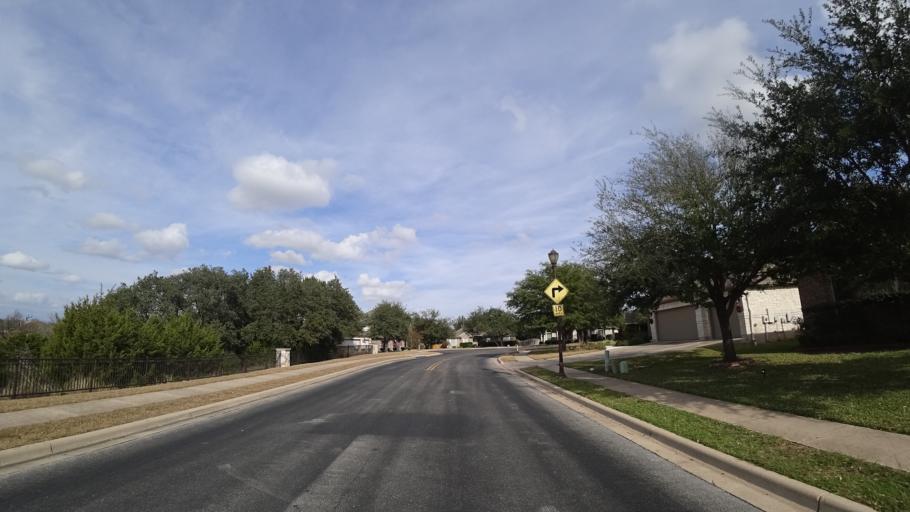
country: US
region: Texas
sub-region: Williamson County
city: Brushy Creek
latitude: 30.5151
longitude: -97.7491
